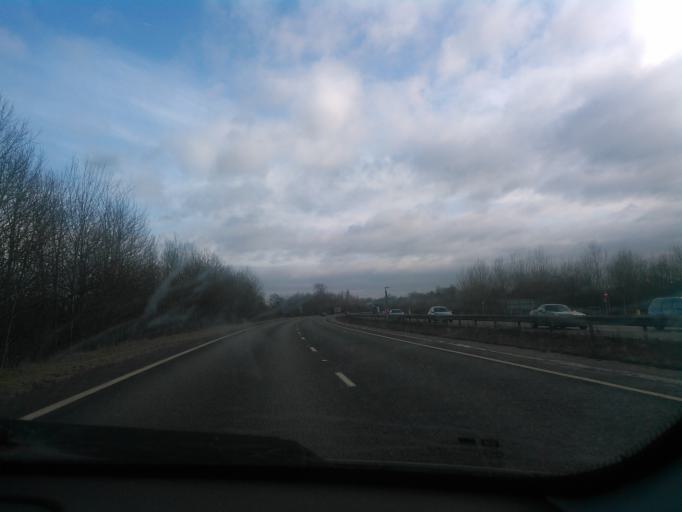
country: GB
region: England
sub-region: Derbyshire
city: Rodsley
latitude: 52.8851
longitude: -1.7321
